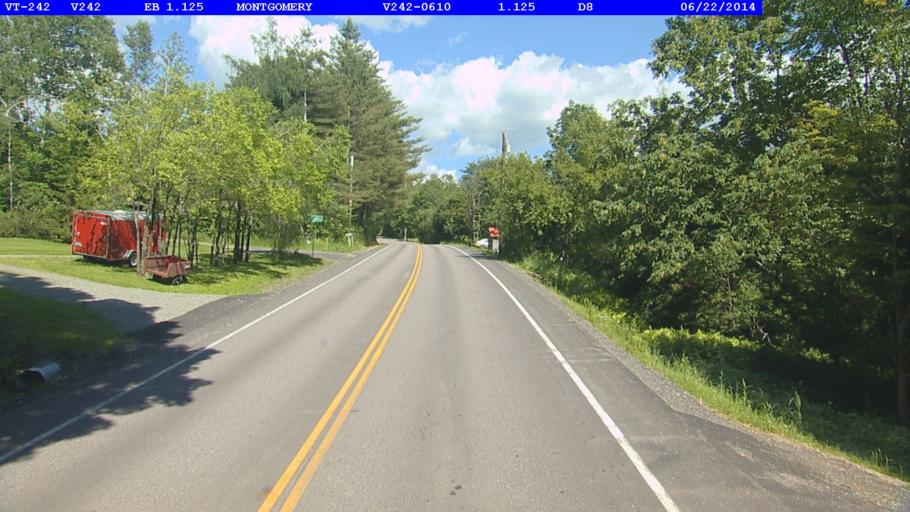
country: US
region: Vermont
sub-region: Franklin County
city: Richford
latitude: 44.8830
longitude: -72.5898
